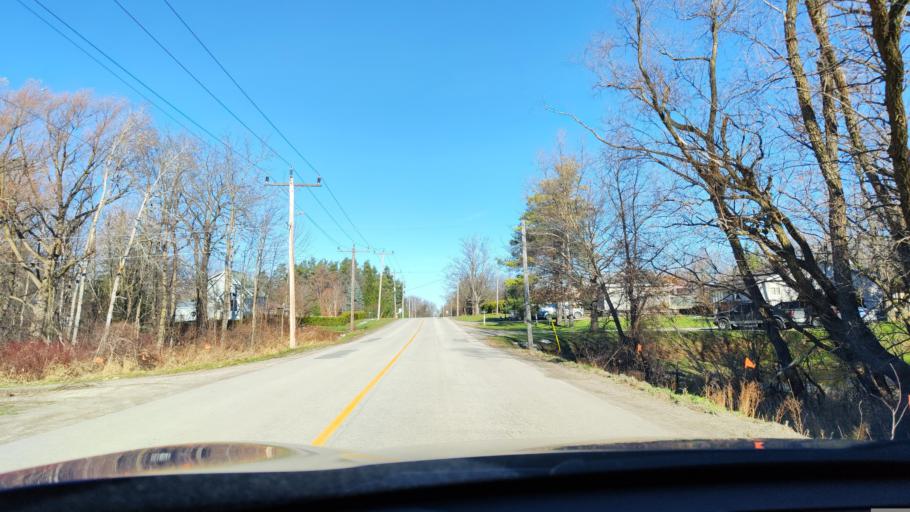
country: CA
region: Ontario
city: Collingwood
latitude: 44.4626
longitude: -80.1733
